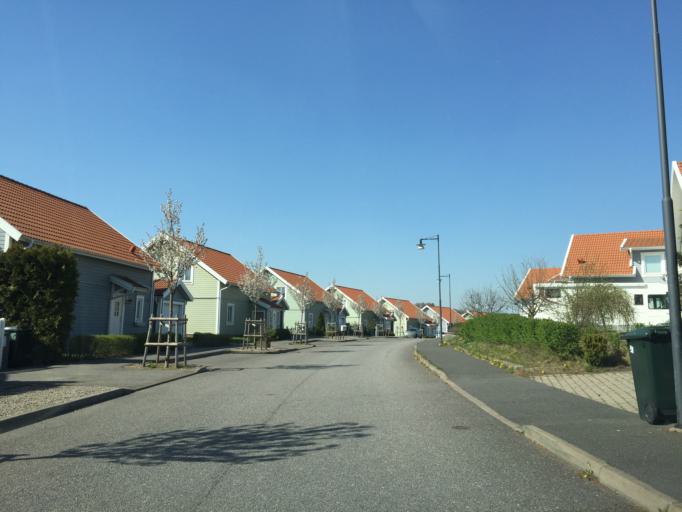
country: SE
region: Vaestra Goetaland
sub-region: Goteborg
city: Hammarkullen
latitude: 57.7888
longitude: 12.0498
